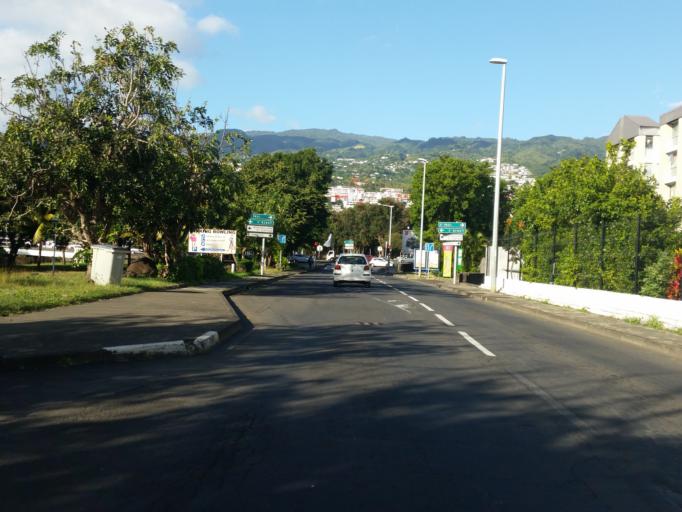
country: RE
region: Reunion
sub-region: Reunion
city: Saint-Denis
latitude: -20.8886
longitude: 55.4640
